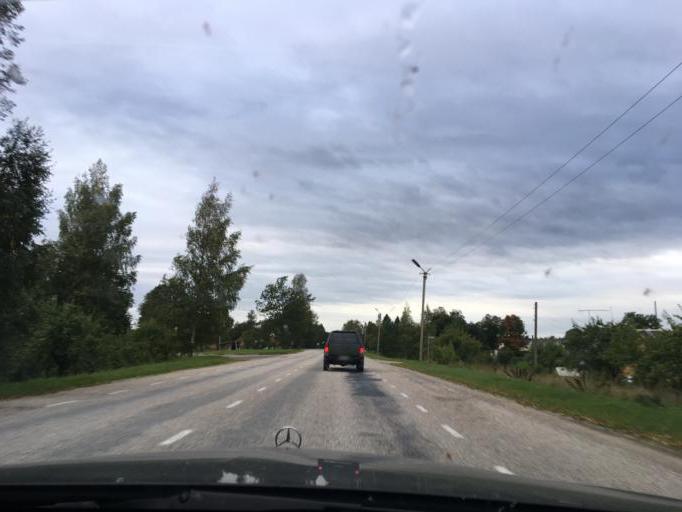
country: LV
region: Aluksnes Rajons
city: Aluksne
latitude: 57.6017
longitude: 27.2319
